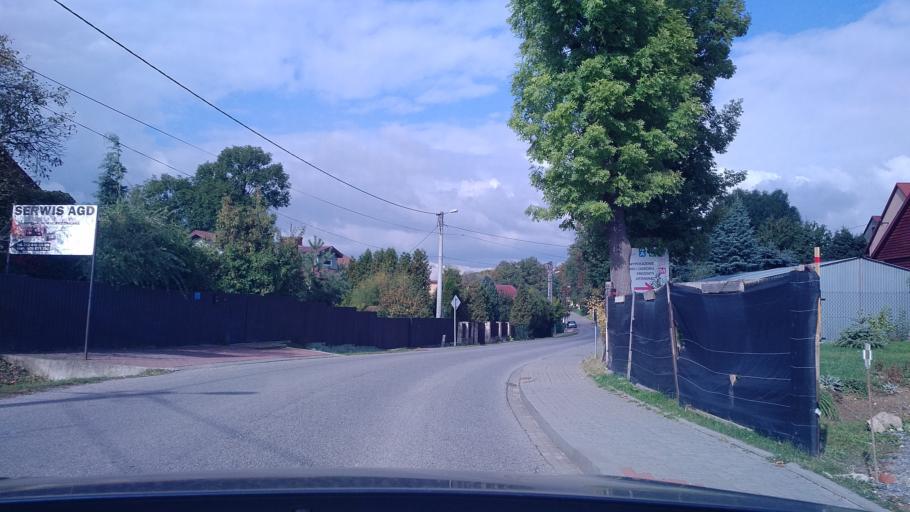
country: PL
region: Lesser Poland Voivodeship
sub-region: Powiat krakowski
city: Modlnica
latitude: 50.1263
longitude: 19.8668
